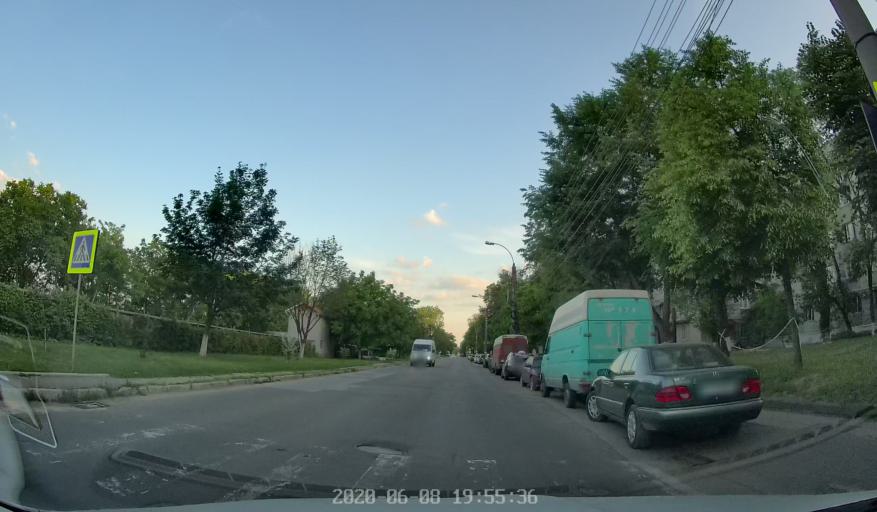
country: MD
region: Chisinau
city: Chisinau
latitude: 47.0277
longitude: 28.8837
